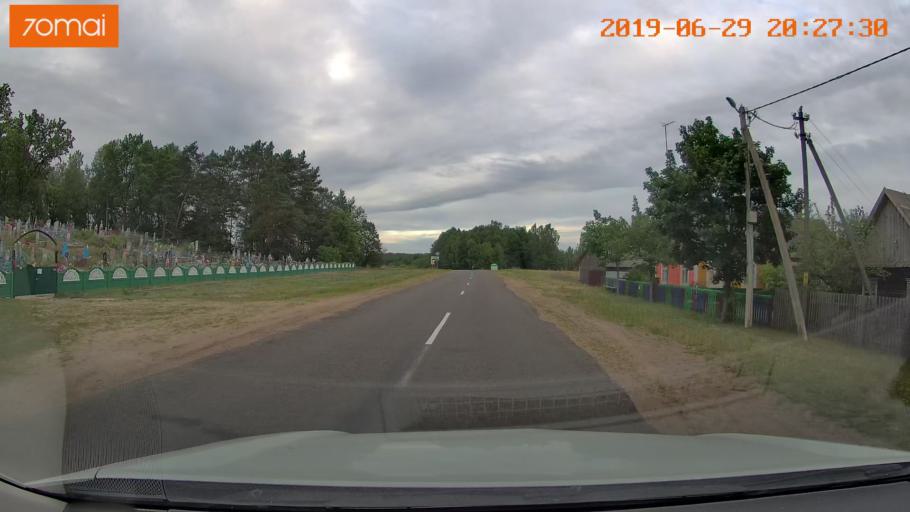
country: BY
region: Brest
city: Hantsavichy
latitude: 52.4742
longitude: 26.3050
